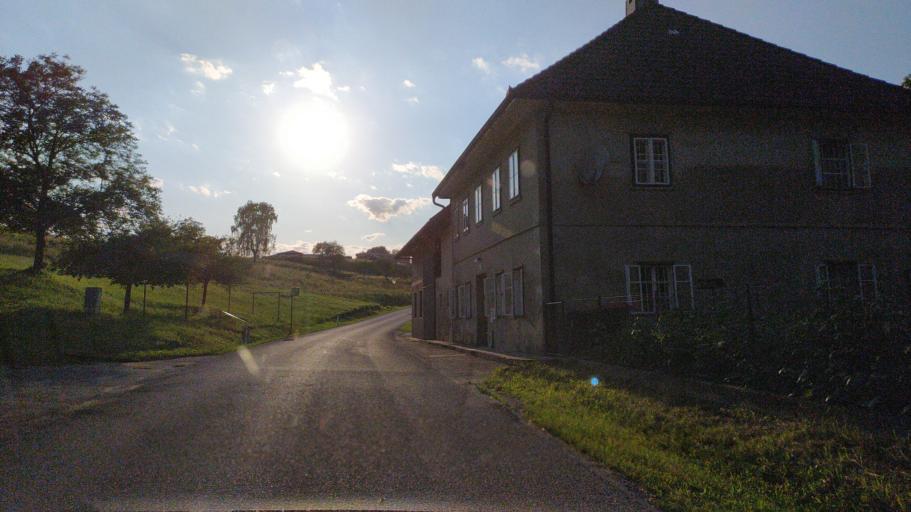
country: AT
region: Lower Austria
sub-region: Politischer Bezirk Amstetten
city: Sankt Valentin
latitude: 48.1986
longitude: 14.5786
